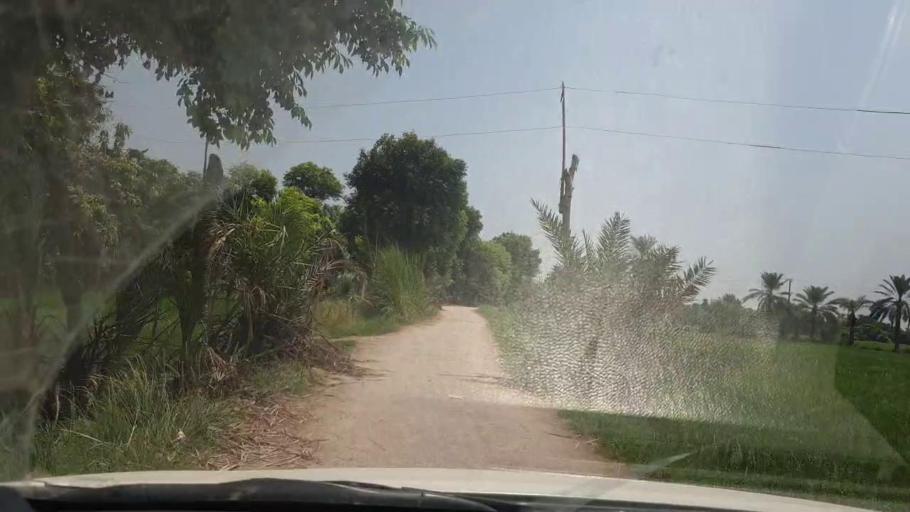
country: PK
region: Sindh
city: Shikarpur
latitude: 27.9324
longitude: 68.6671
